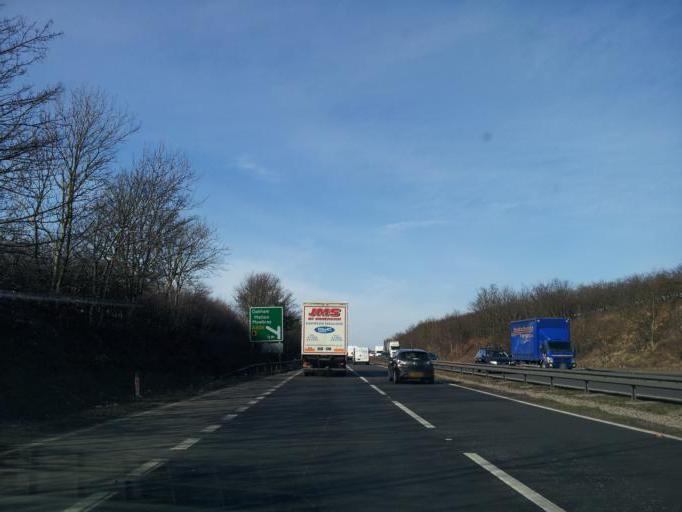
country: GB
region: England
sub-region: District of Rutland
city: Tinwell
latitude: 52.6478
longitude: -0.5068
